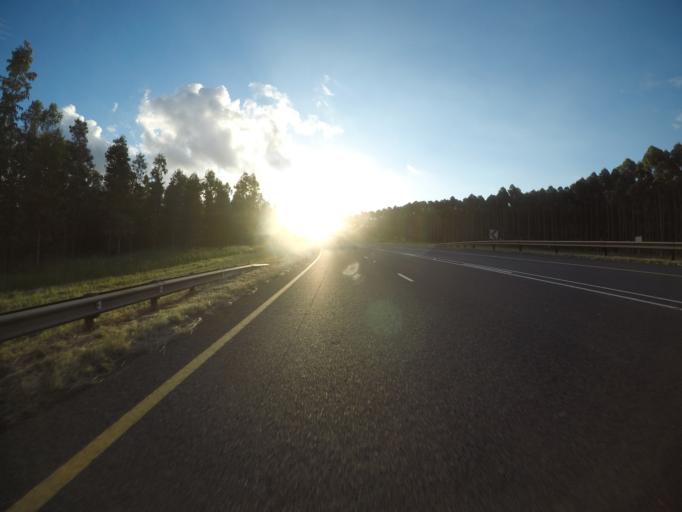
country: ZA
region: KwaZulu-Natal
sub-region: uThungulu District Municipality
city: Richards Bay
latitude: -28.6882
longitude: 31.9963
